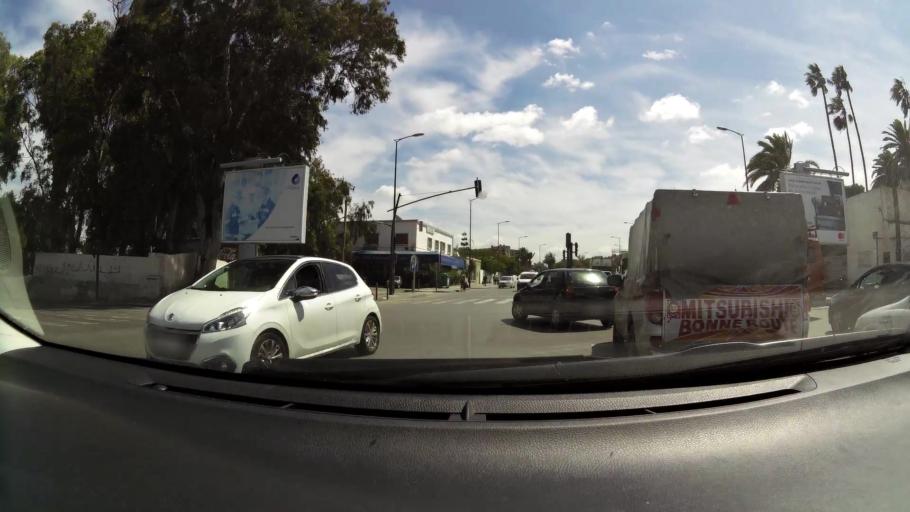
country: MA
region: Grand Casablanca
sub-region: Mediouna
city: Tit Mellil
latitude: 33.6046
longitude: -7.5373
